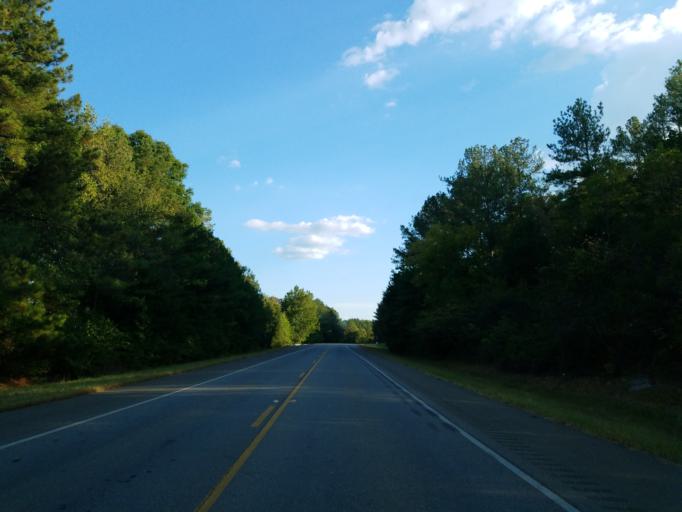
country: US
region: Georgia
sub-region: Murray County
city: Chatsworth
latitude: 34.6429
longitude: -84.7152
